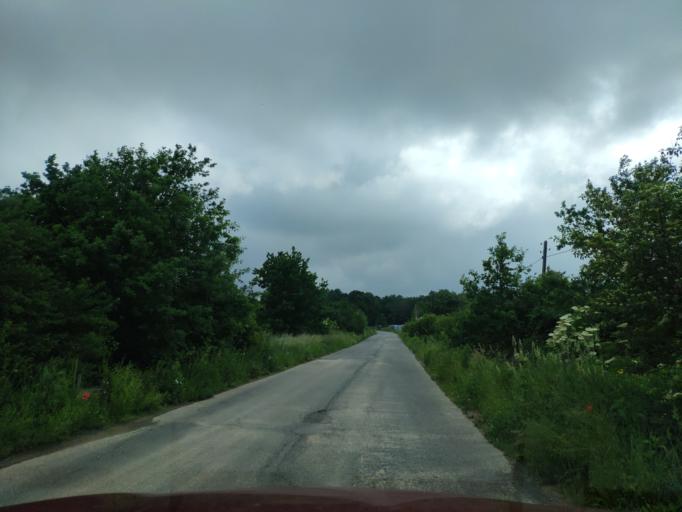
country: SK
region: Presovsky
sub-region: Okres Presov
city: Presov
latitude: 48.9980
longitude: 21.3046
